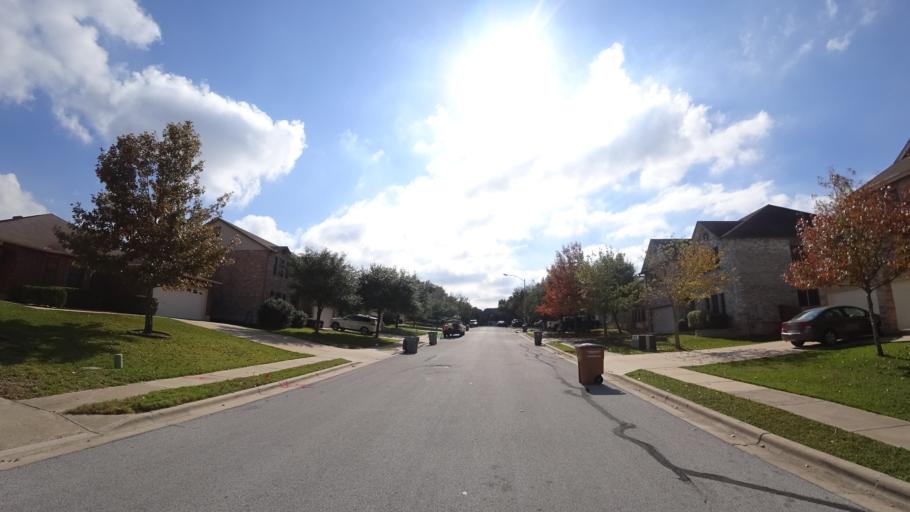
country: US
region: Texas
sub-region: Travis County
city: Shady Hollow
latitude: 30.1583
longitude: -97.8455
